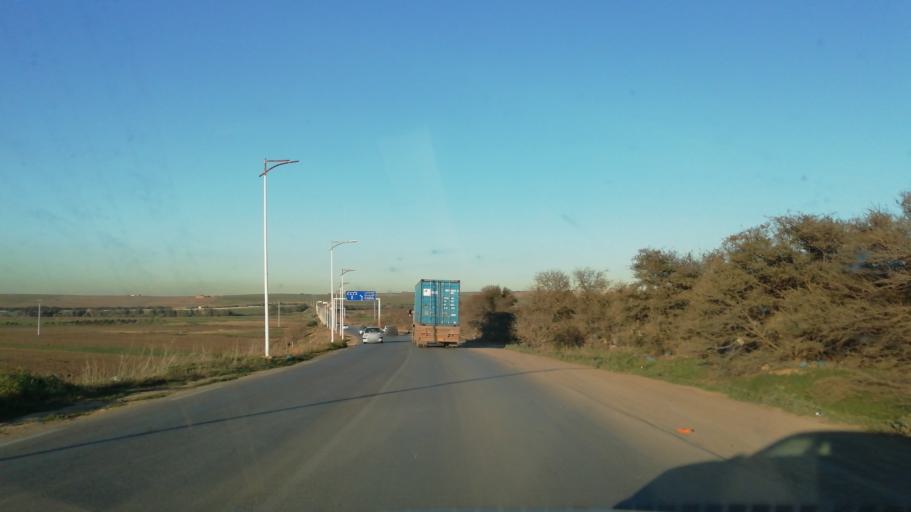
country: DZ
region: Oran
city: Sidi ech Chahmi
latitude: 35.5649
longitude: -0.5611
